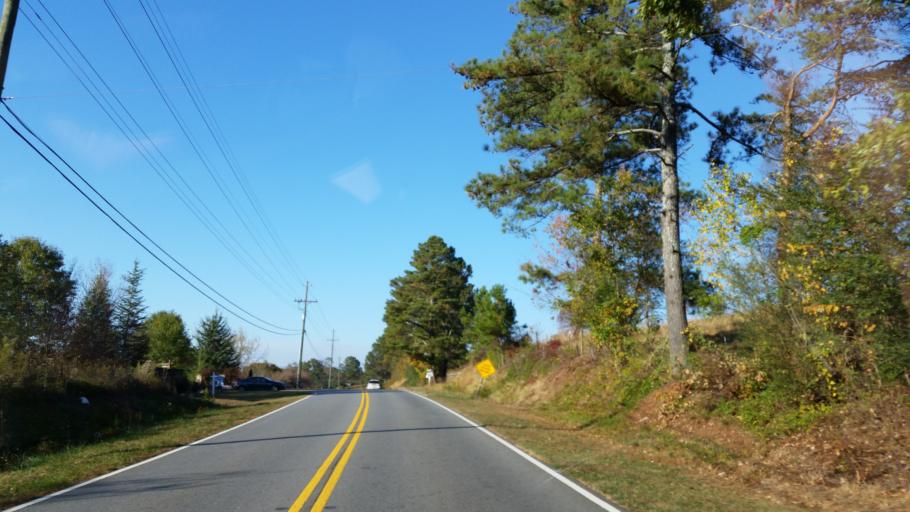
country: US
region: Georgia
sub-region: Gilmer County
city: Ellijay
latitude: 34.6482
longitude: -84.4693
